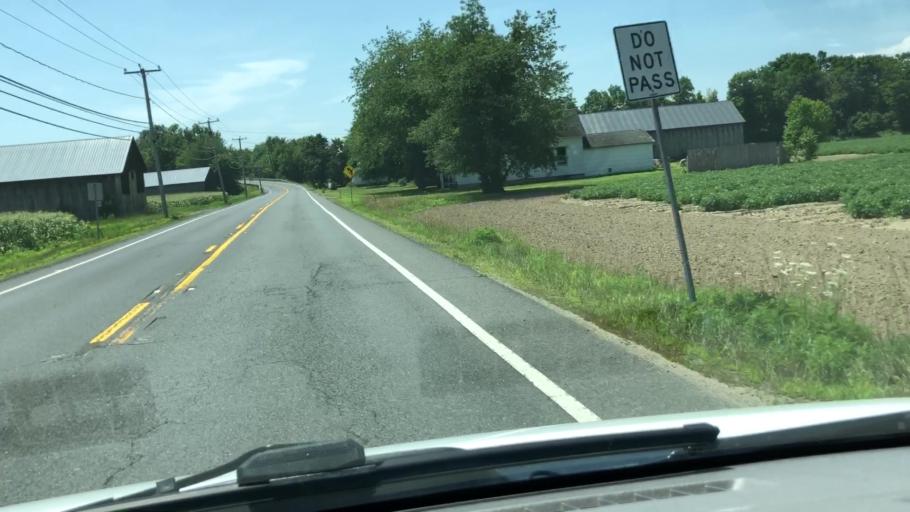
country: US
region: Massachusetts
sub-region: Franklin County
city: Whately
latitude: 42.4359
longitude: -72.6238
